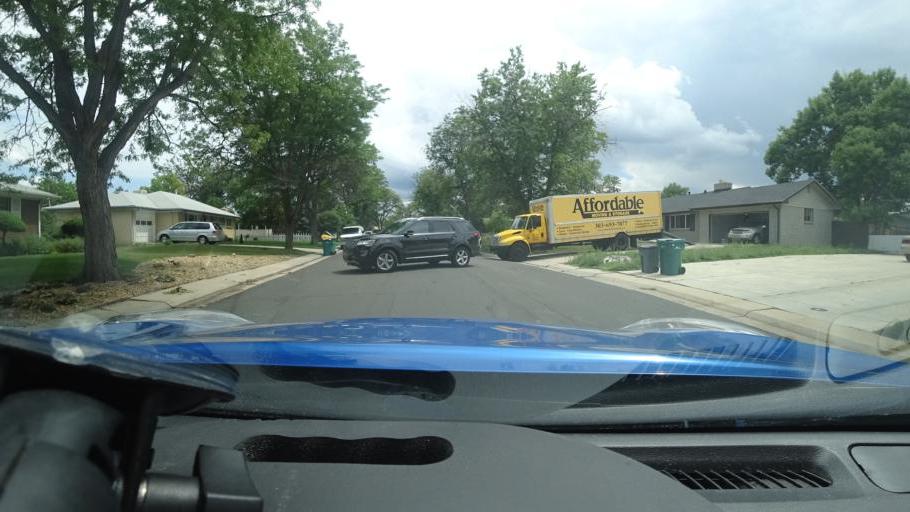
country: US
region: Colorado
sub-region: Adams County
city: Aurora
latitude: 39.7248
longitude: -104.8333
